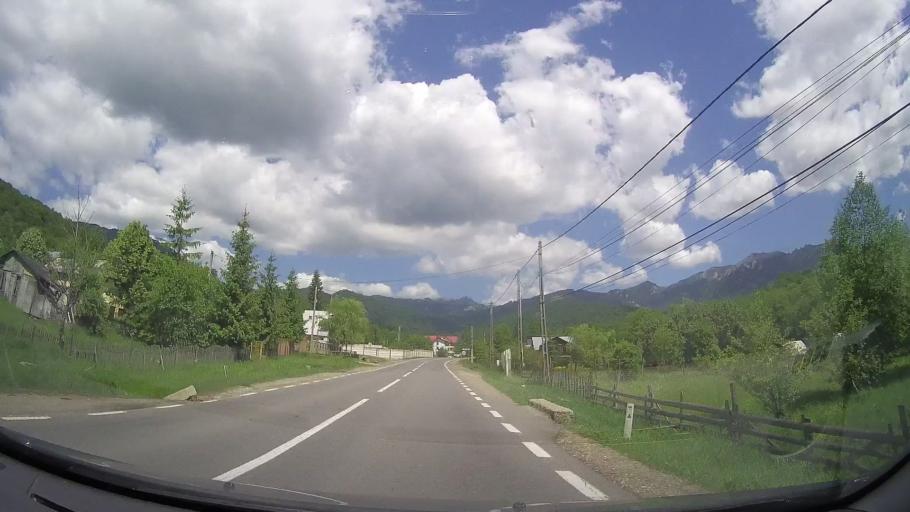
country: RO
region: Prahova
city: Maneciu
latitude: 45.4481
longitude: 25.9368
